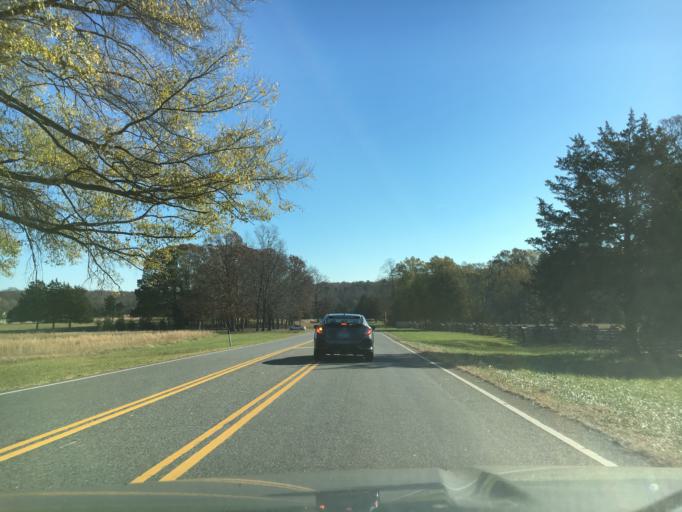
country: US
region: Virginia
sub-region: Appomattox County
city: Appomattox
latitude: 37.3751
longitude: -78.8002
